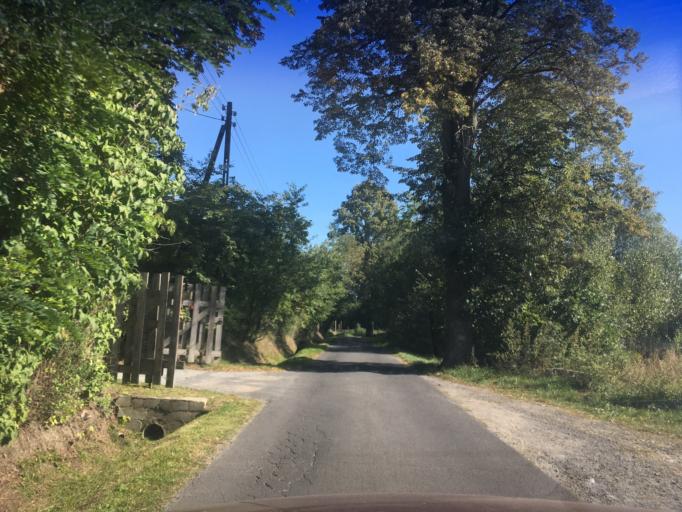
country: PL
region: Lower Silesian Voivodeship
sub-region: Powiat lubanski
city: Swieradow-Zdroj
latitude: 50.9585
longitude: 15.3143
